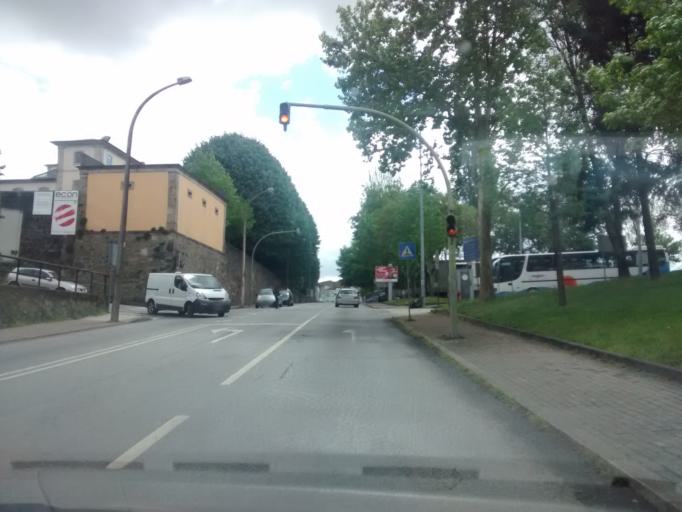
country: PT
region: Braga
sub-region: Braga
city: Braga
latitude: 41.5536
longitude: -8.4302
